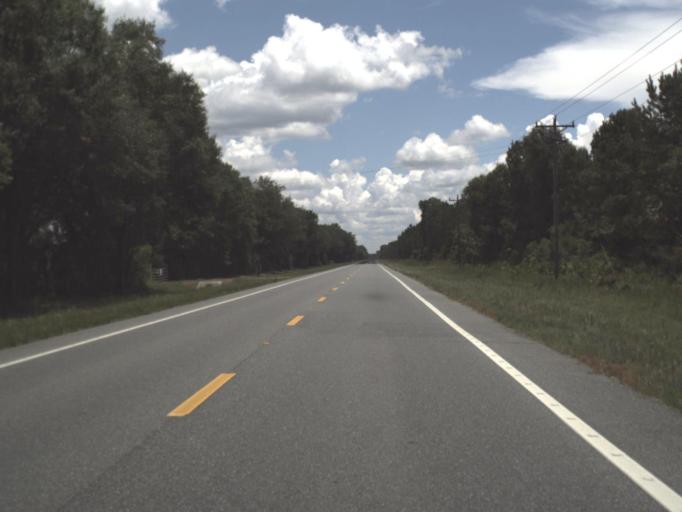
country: US
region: Florida
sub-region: Taylor County
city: Perry
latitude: 30.1411
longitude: -83.9168
